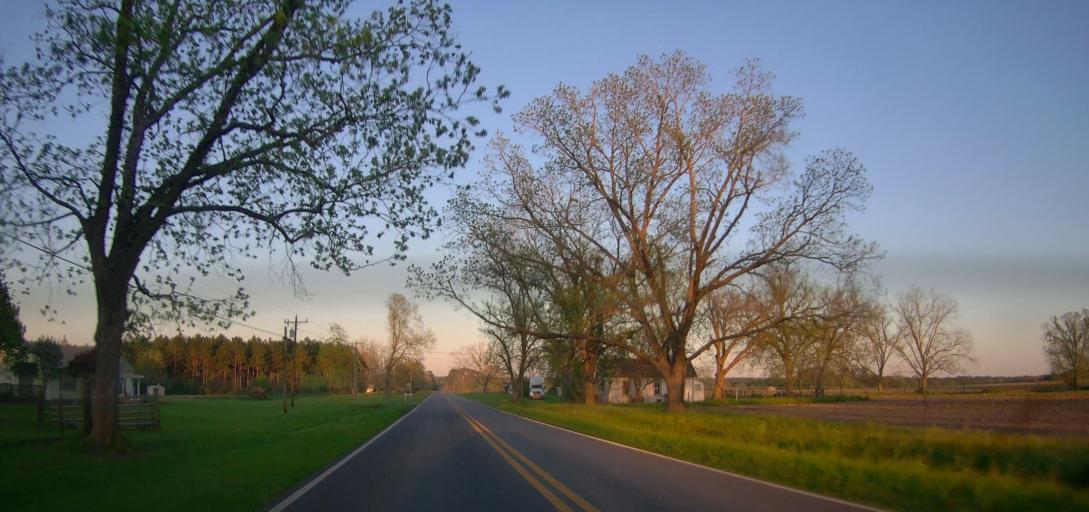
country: US
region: Georgia
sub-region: Ben Hill County
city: Fitzgerald
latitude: 31.7180
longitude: -83.3090
